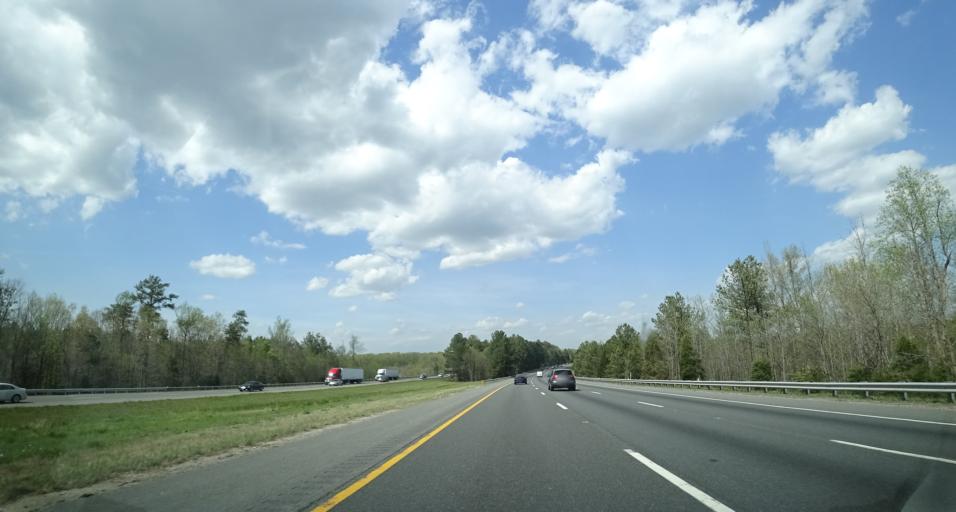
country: US
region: Virginia
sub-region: Spotsylvania County
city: Spotsylvania Courthouse
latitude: 38.1600
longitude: -77.5073
